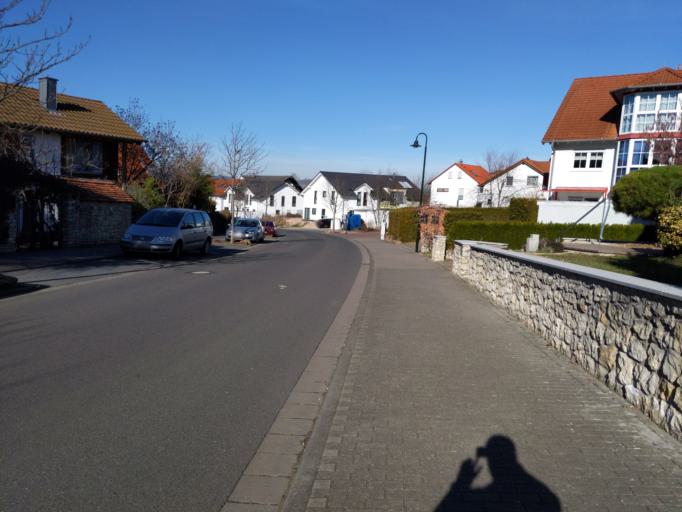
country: DE
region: Rheinland-Pfalz
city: Nieder-Ingelheim
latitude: 49.9793
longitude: 8.0782
